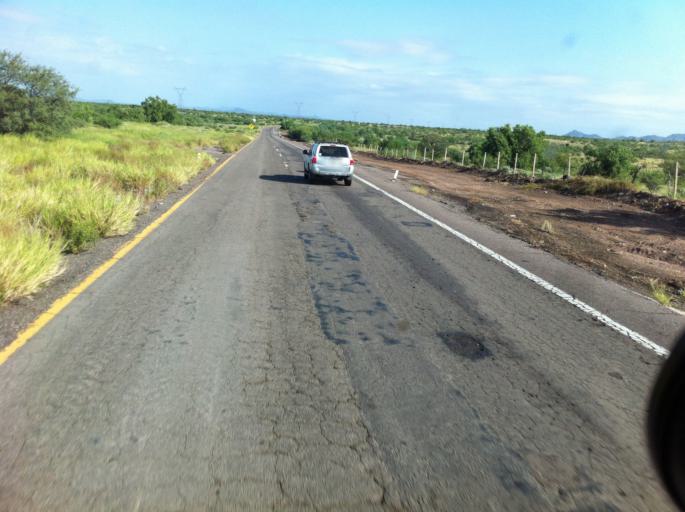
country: MX
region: Sonora
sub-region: Hermosillo
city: Miguel Aleman (La Doce)
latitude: 28.5204
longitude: -111.0463
